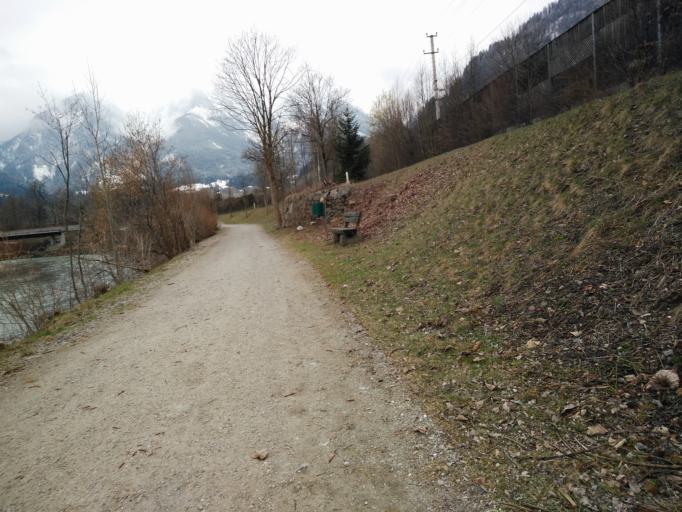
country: AT
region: Salzburg
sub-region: Politischer Bezirk Sankt Johann im Pongau
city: Sankt Johann im Pongau
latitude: 47.3414
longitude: 13.1932
